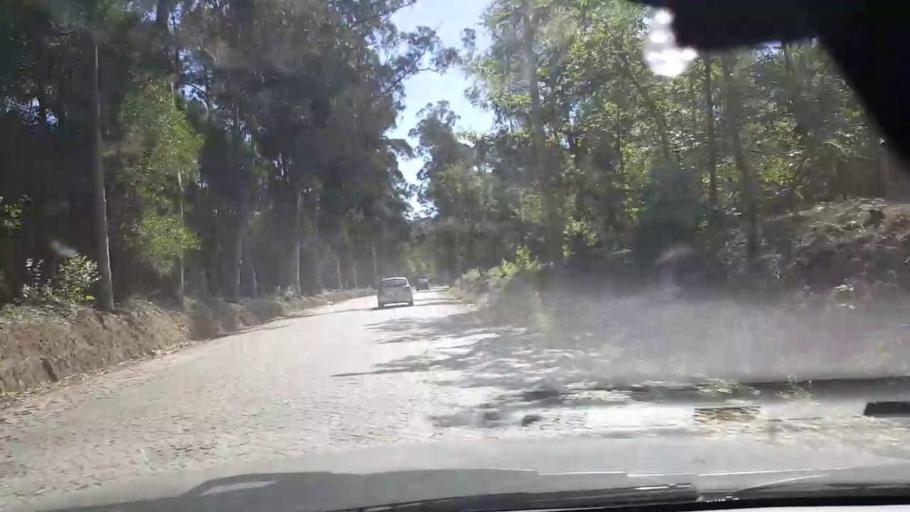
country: PT
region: Porto
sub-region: Vila do Conde
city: Arvore
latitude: 41.3245
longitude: -8.7257
